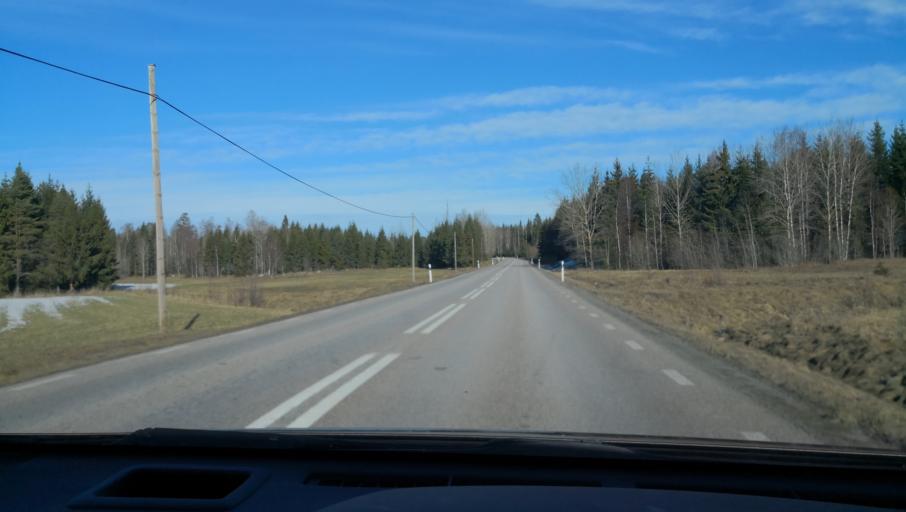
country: SE
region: Uppsala
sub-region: Osthammars Kommun
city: Osterbybruk
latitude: 60.1244
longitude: 17.8084
